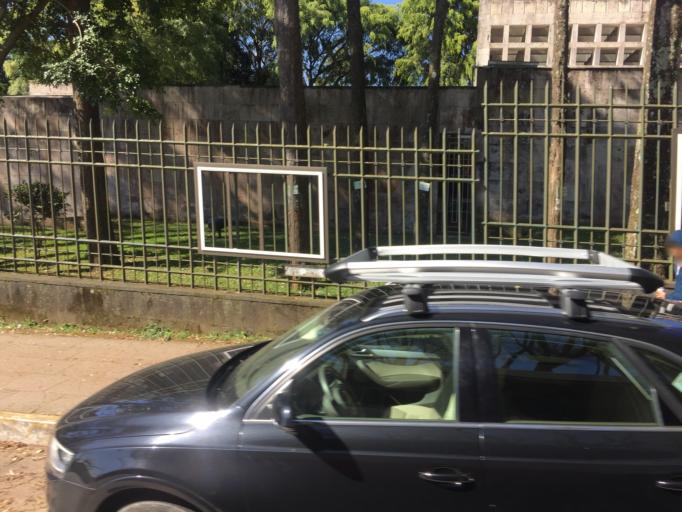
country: MX
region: Veracruz
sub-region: Xalapa
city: Xalapa de Enriquez
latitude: 19.5497
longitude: -96.9319
